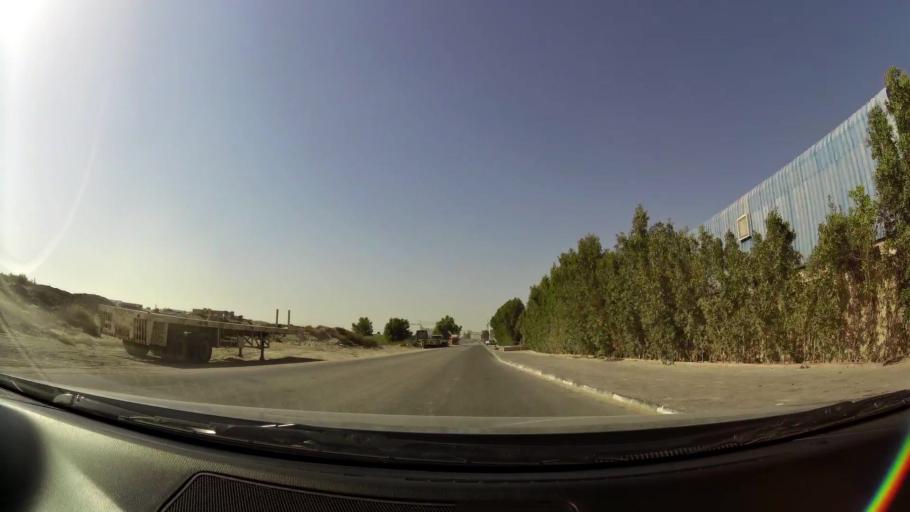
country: AE
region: Dubai
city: Dubai
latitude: 24.9928
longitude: 55.0991
